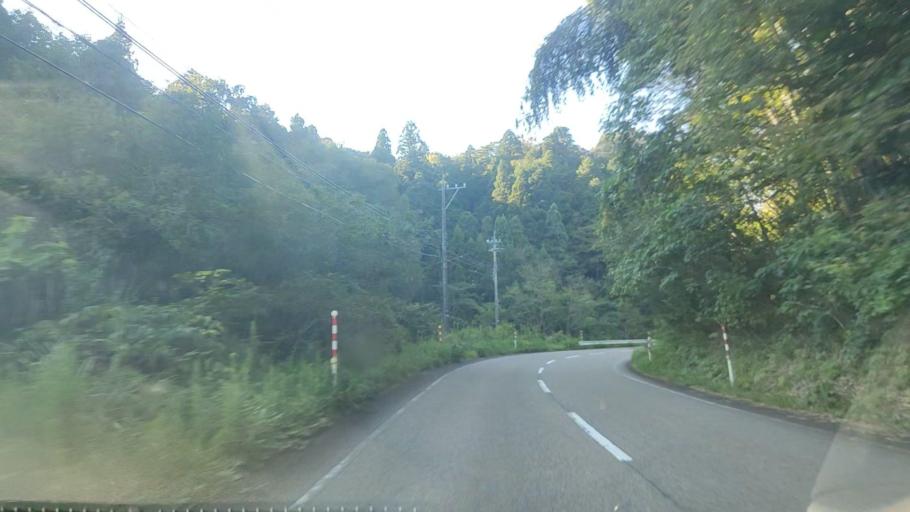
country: JP
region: Ishikawa
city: Nanao
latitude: 37.1159
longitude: 136.9655
